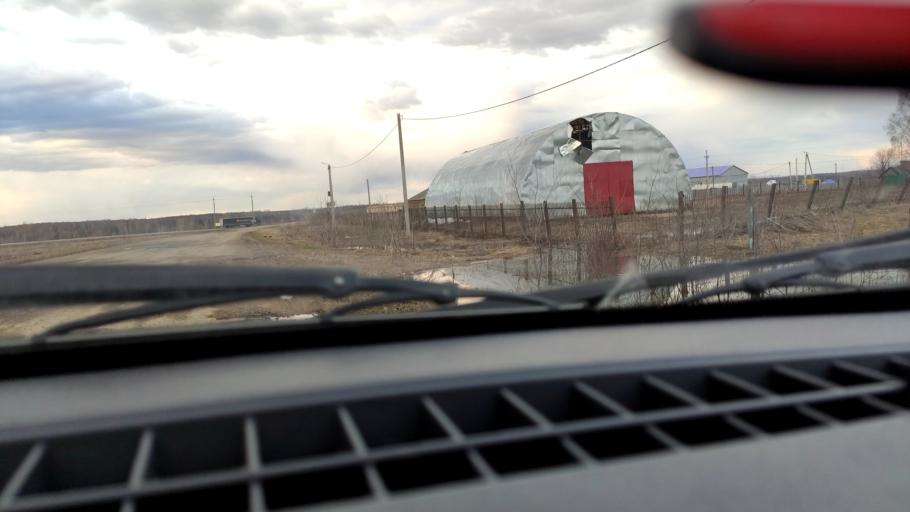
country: RU
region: Bashkortostan
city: Kudeyevskiy
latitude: 54.8145
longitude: 56.7549
